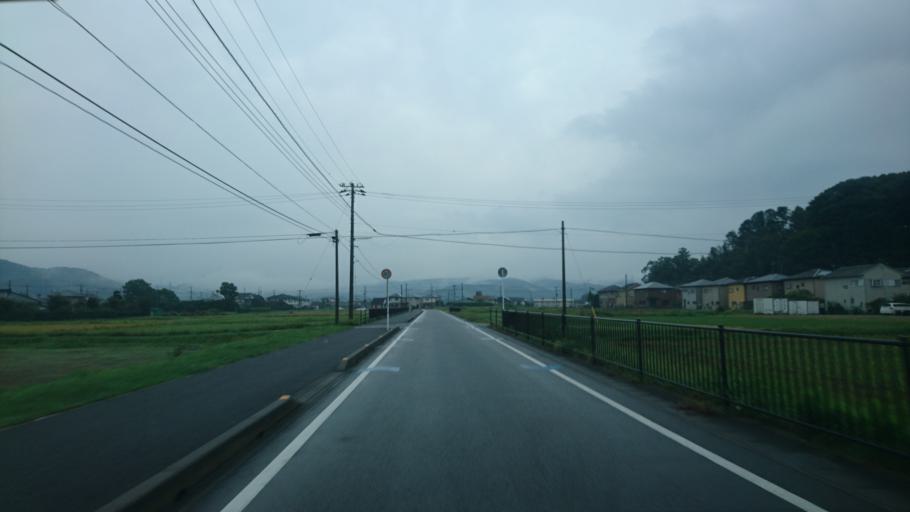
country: JP
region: Chiba
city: Kimitsu
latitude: 35.3036
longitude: 139.9643
